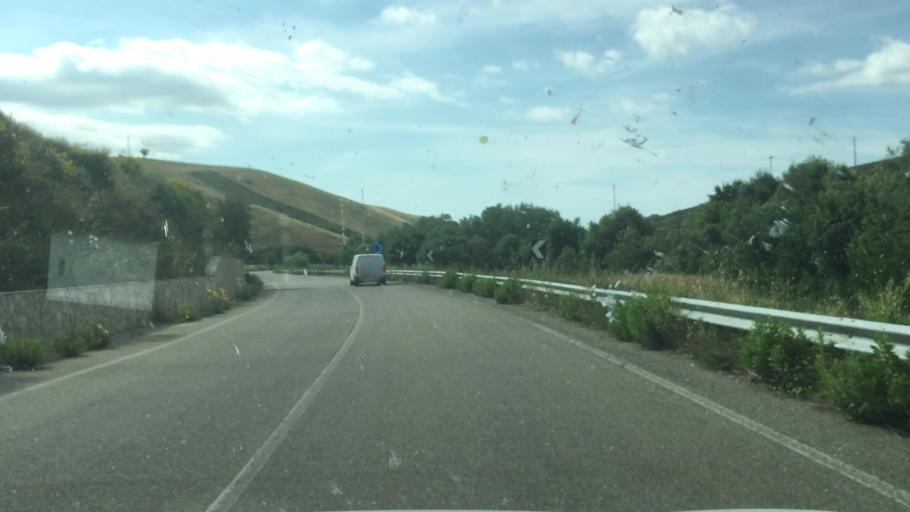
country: IT
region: Basilicate
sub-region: Provincia di Matera
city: Salandra
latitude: 40.5309
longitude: 16.2886
